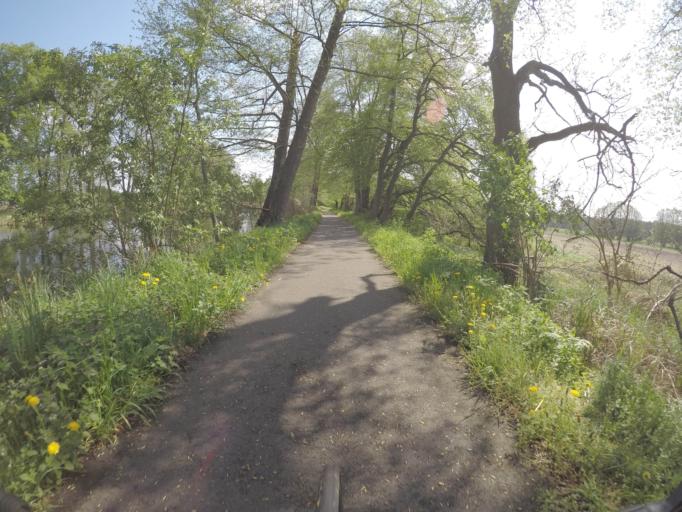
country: DE
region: Brandenburg
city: Marienwerder
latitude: 52.8376
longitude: 13.5871
